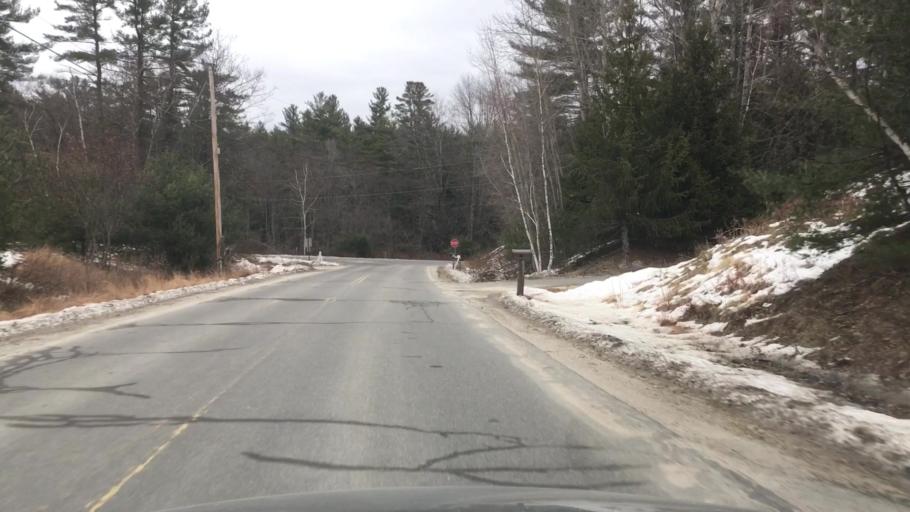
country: US
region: New Hampshire
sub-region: Hillsborough County
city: New Boston
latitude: 43.0000
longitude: -71.6618
